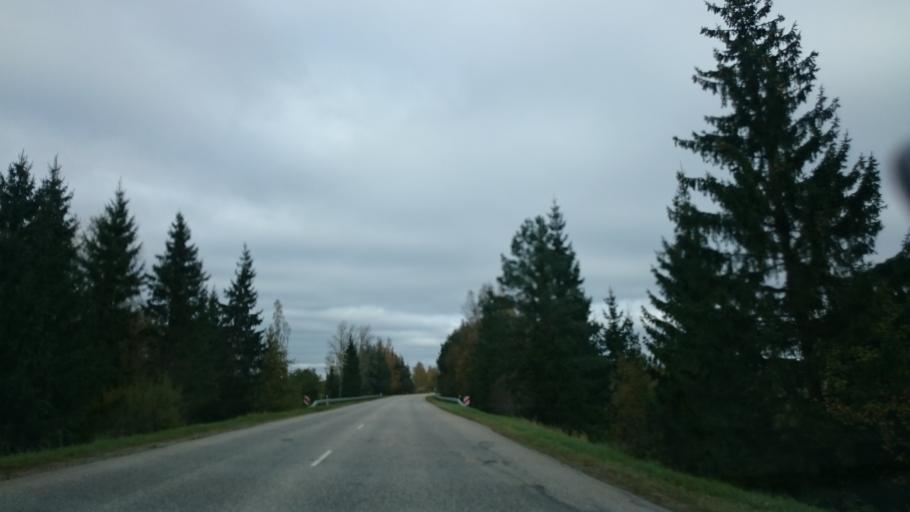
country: LV
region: Amatas Novads
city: Drabesi
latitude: 57.2312
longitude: 25.2539
